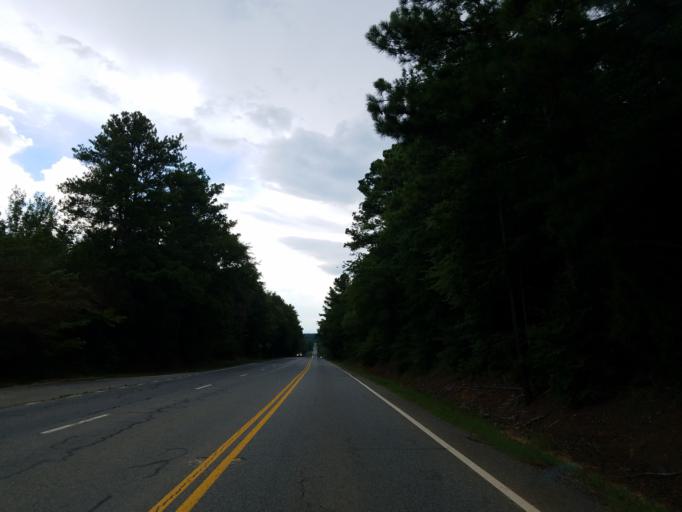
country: US
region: Georgia
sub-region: Bartow County
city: Adairsville
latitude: 34.3281
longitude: -84.8999
